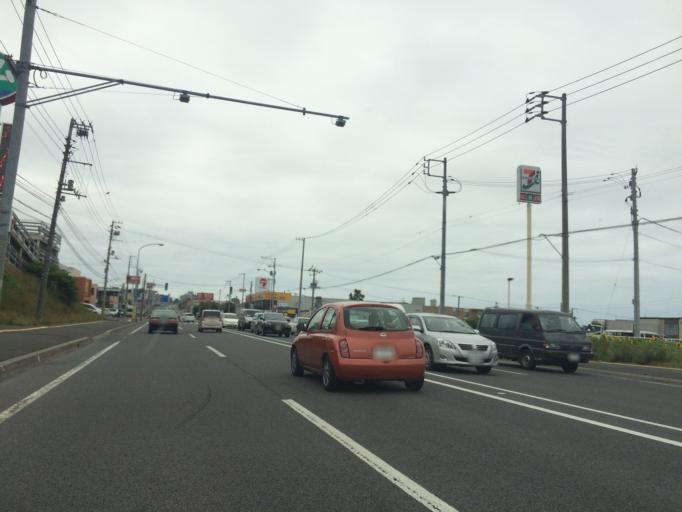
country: JP
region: Hokkaido
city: Sapporo
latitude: 43.1240
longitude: 141.2232
